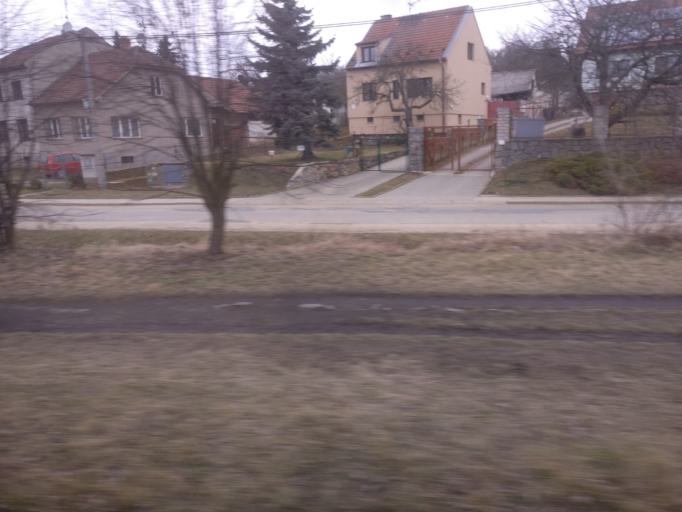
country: CZ
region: South Moravian
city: Strelice
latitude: 49.1544
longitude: 16.4867
